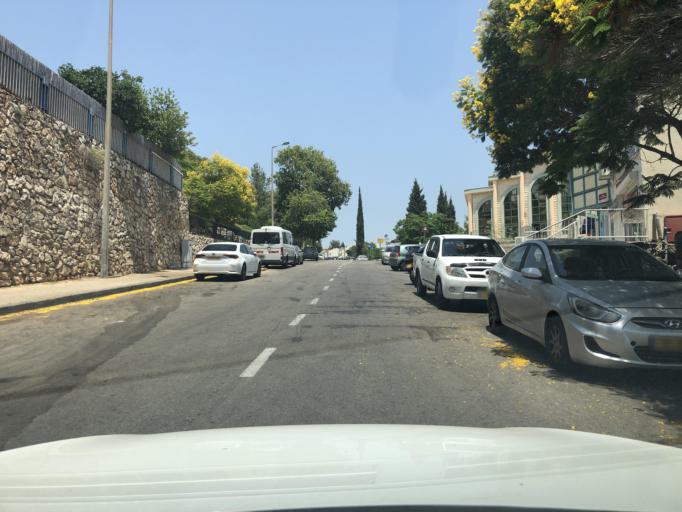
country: IL
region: Haifa
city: Daliyat el Karmil
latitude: 32.6475
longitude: 35.0932
